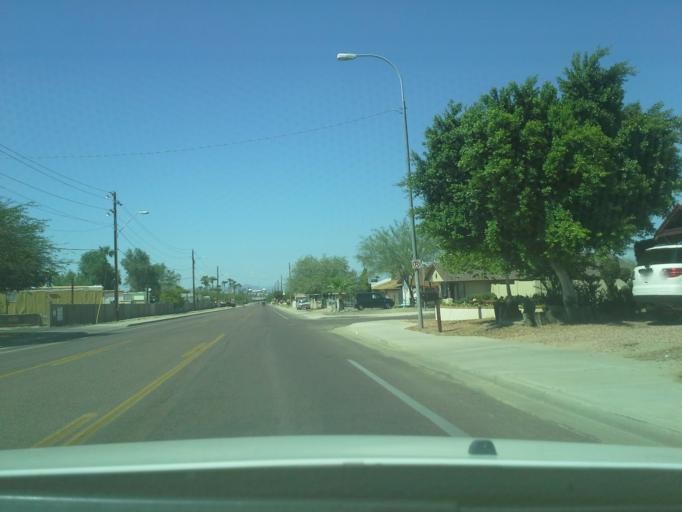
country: US
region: Arizona
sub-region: Maricopa County
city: Phoenix
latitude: 33.3685
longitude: -112.0659
